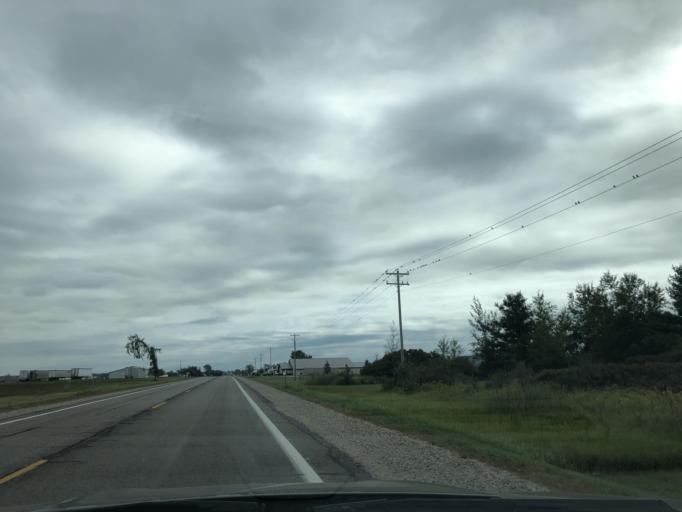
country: US
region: Michigan
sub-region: Missaukee County
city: Lake City
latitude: 44.1936
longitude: -85.1728
